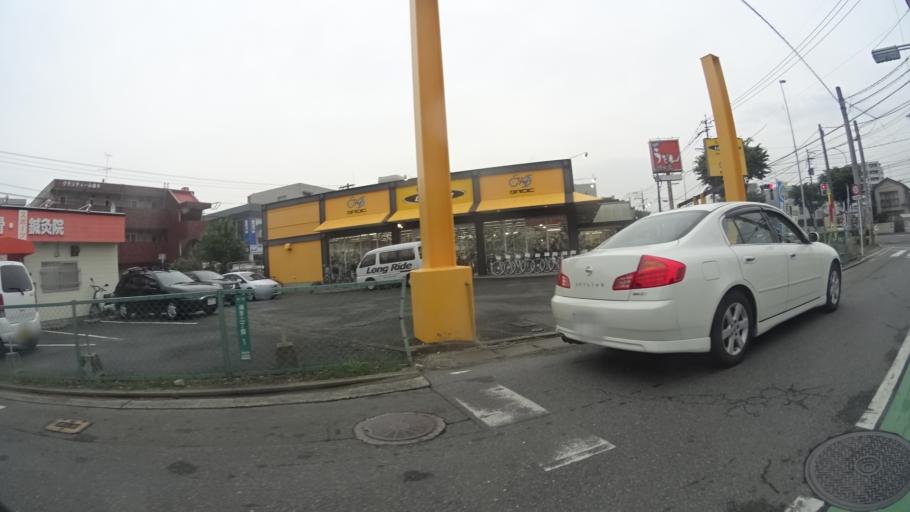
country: JP
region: Fukuoka
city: Onojo
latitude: 33.5507
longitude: 130.4388
